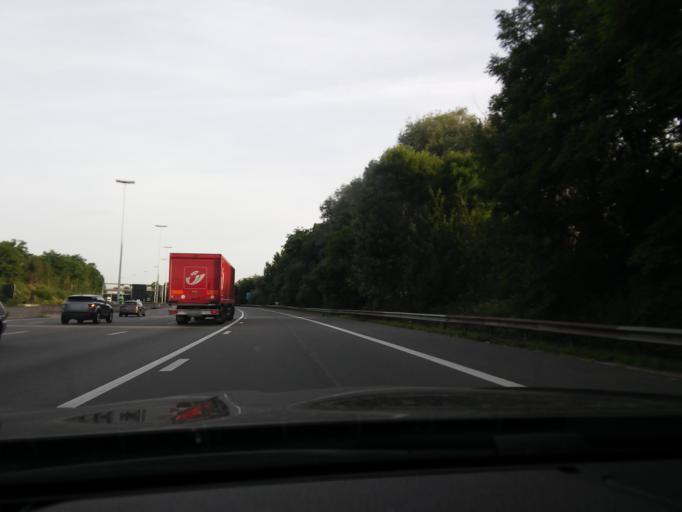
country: BE
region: Flanders
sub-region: Provincie Antwerpen
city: Edegem
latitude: 51.1667
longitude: 4.4130
